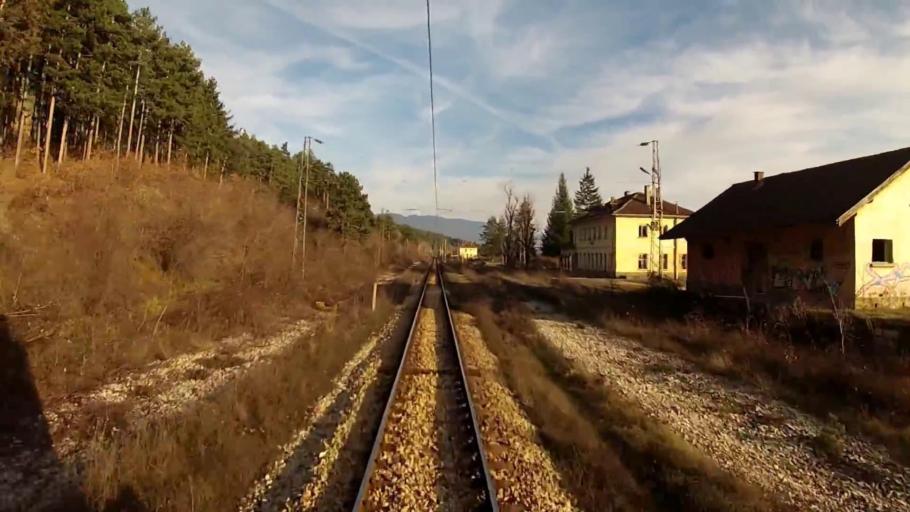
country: BG
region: Plovdiv
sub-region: Obshtina Karlovo
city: Klisura
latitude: 42.7229
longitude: 24.5911
